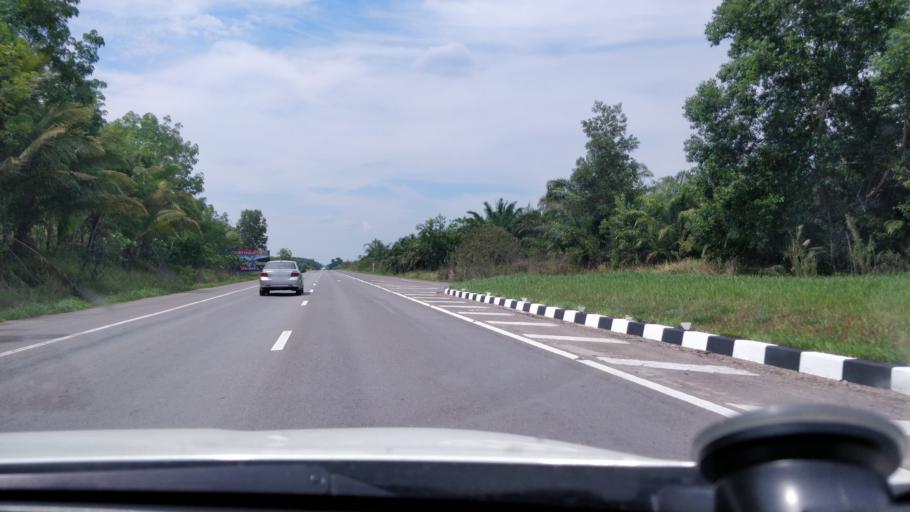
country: TH
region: Surat Thani
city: Khian Sa
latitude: 8.7453
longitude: 99.1607
